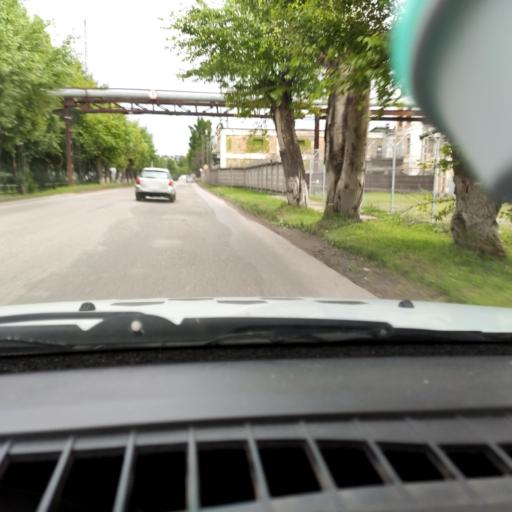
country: RU
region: Perm
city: Chusovoy
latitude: 58.2937
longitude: 57.8148
